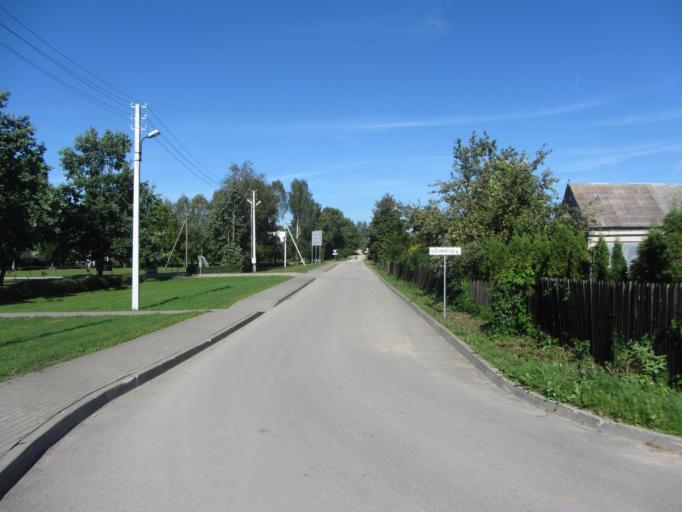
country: LT
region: Alytaus apskritis
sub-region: Alytus
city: Alytus
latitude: 54.4378
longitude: 23.9925
